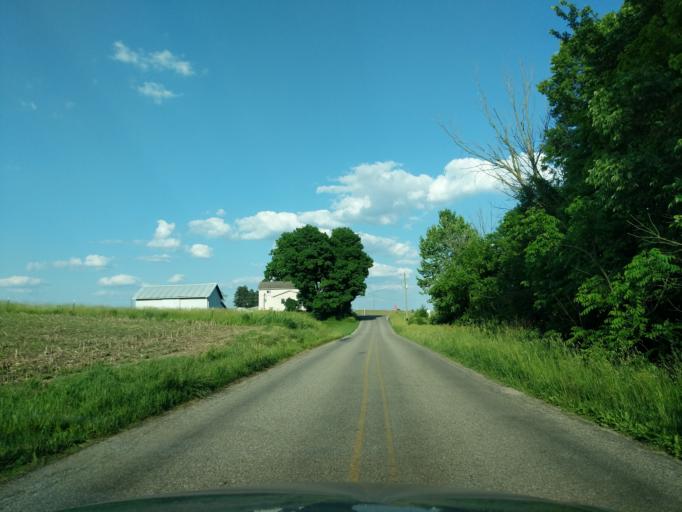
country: US
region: Indiana
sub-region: Whitley County
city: Tri-Lakes
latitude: 41.3025
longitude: -85.5476
